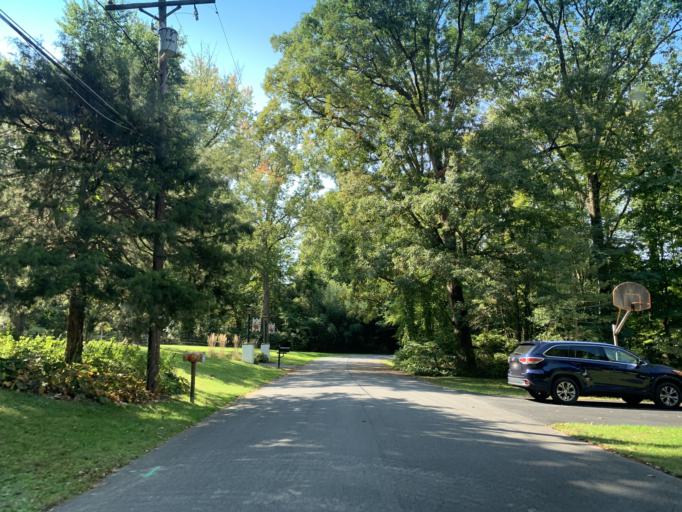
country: US
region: Maryland
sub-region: Harford County
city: South Bel Air
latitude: 39.5242
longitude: -76.3338
